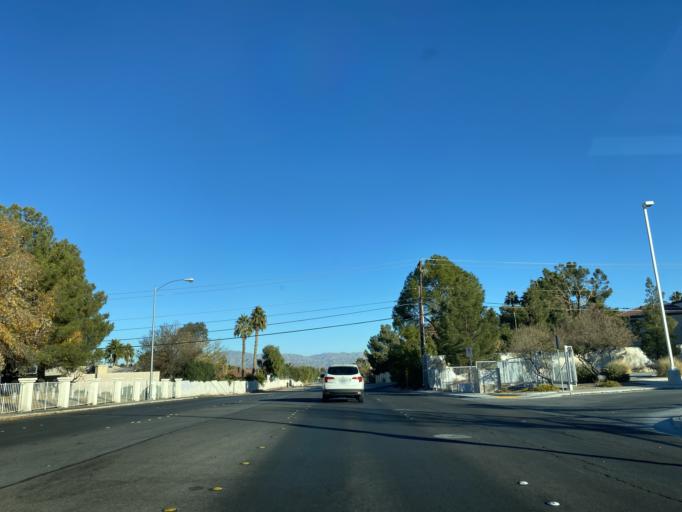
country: US
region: Nevada
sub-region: Clark County
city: Winchester
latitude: 36.1163
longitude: -115.1098
